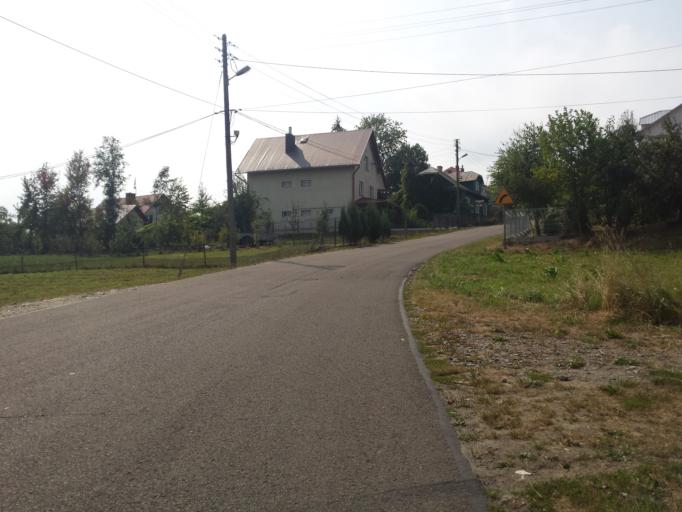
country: PL
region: Subcarpathian Voivodeship
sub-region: Powiat rzeszowski
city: Dynow
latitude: 49.8187
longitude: 22.2117
